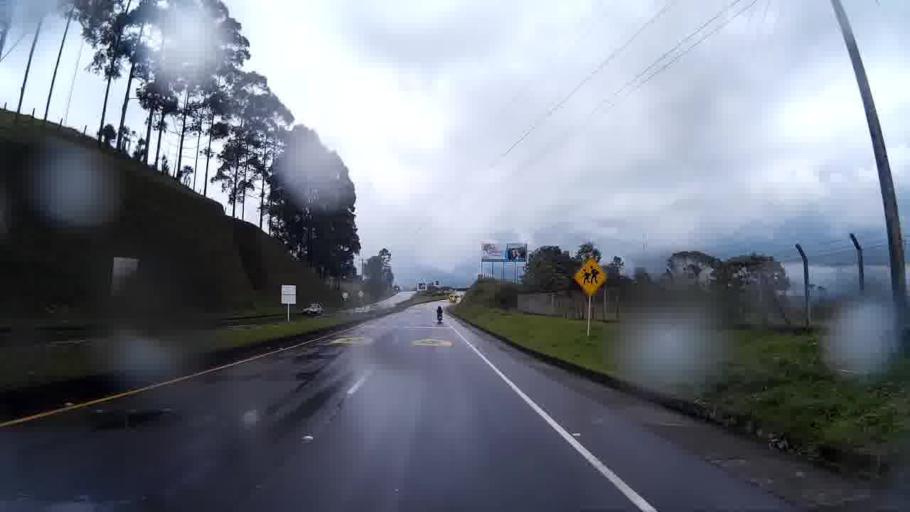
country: CO
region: Quindio
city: Salento
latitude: 4.6773
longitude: -75.6026
